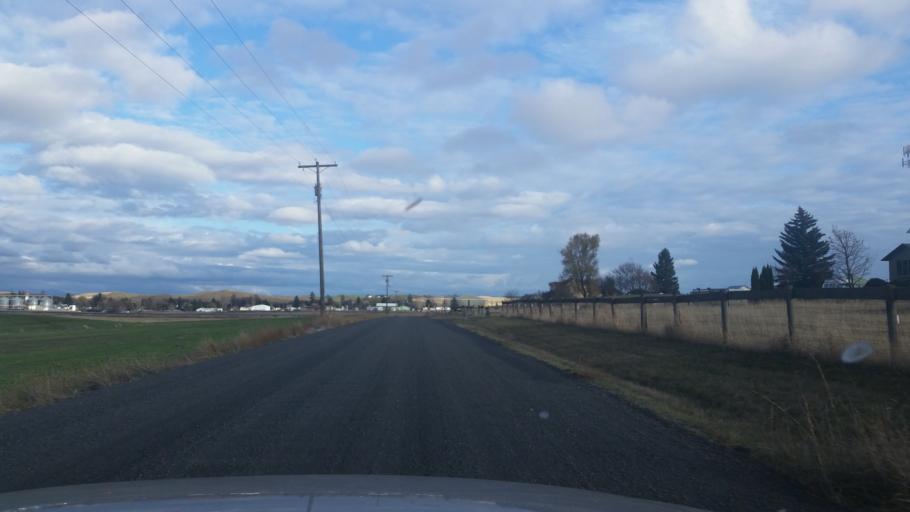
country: US
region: Washington
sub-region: Spokane County
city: Cheney
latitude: 47.4274
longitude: -117.3938
